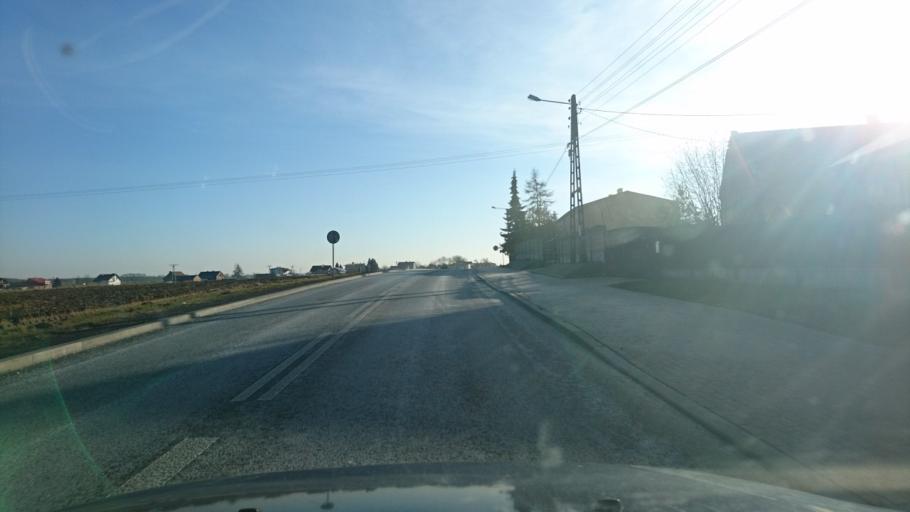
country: PL
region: Silesian Voivodeship
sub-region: Powiat klobucki
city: Starokrzepice
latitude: 51.0202
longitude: 18.6517
